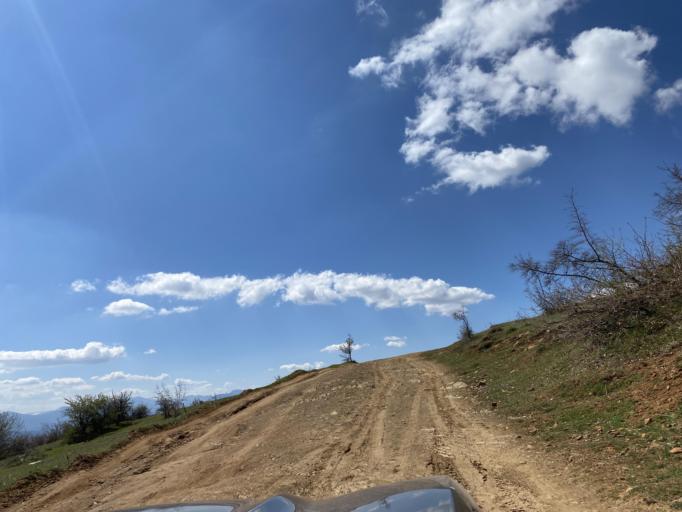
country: MK
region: Caska
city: Caska
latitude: 41.7290
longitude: 21.6638
